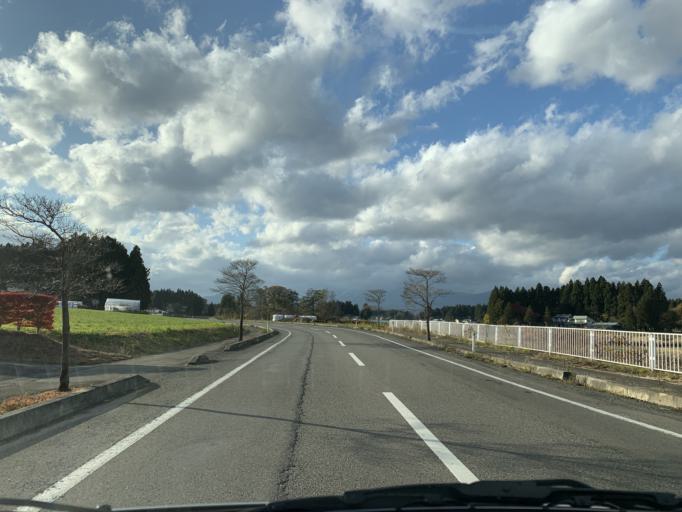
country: JP
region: Iwate
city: Mizusawa
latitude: 39.1128
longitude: 141.0668
